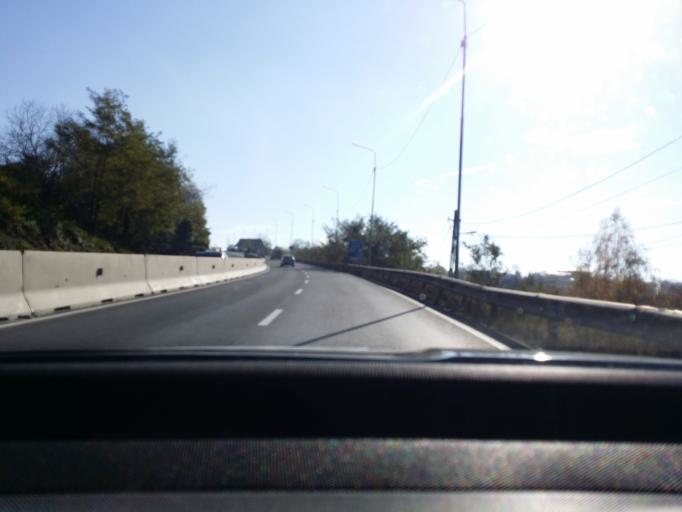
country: RO
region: Prahova
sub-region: Comuna Banesti
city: Banesti
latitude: 45.1024
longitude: 25.7561
